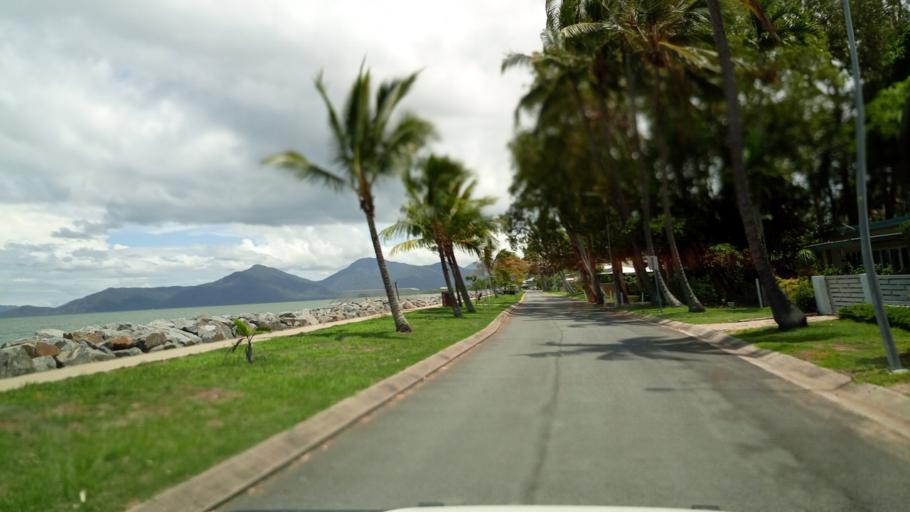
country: AU
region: Queensland
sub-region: Cairns
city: Yorkeys Knob
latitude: -16.8479
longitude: 145.7470
